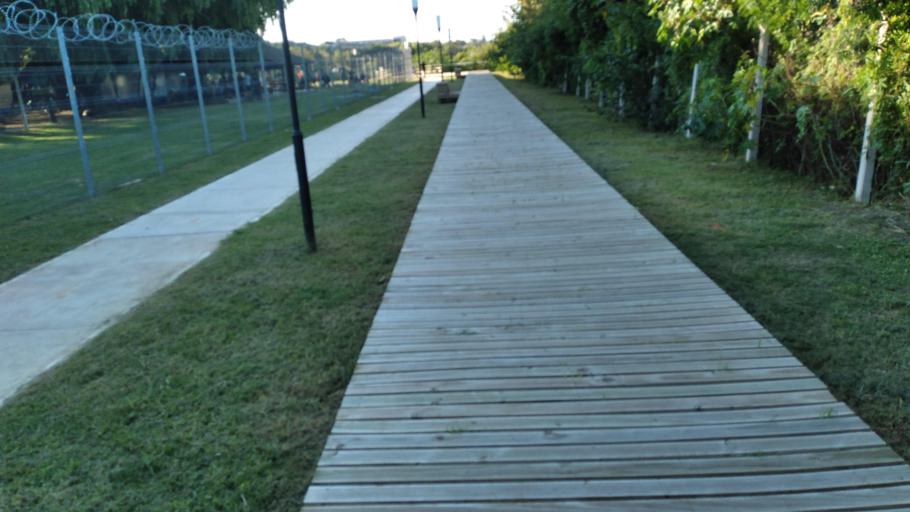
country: AR
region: Buenos Aires
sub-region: Partido de Vicente Lopez
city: Olivos
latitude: -34.4984
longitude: -58.4785
